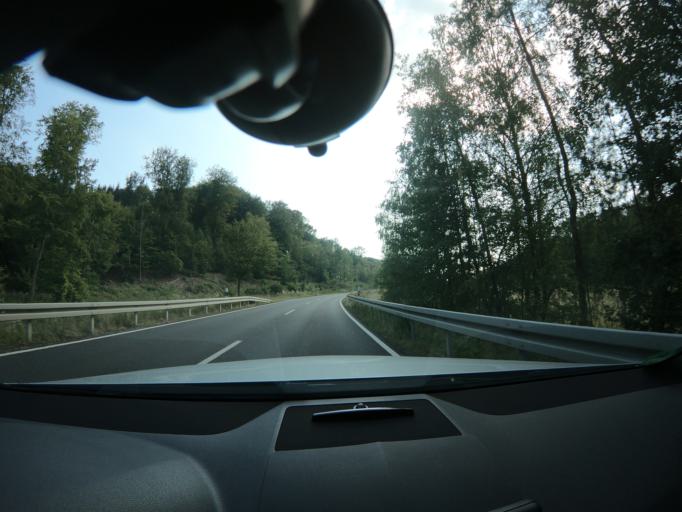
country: DE
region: Hesse
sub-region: Regierungsbezirk Giessen
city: Kirchhain
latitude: 50.8527
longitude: 8.9348
